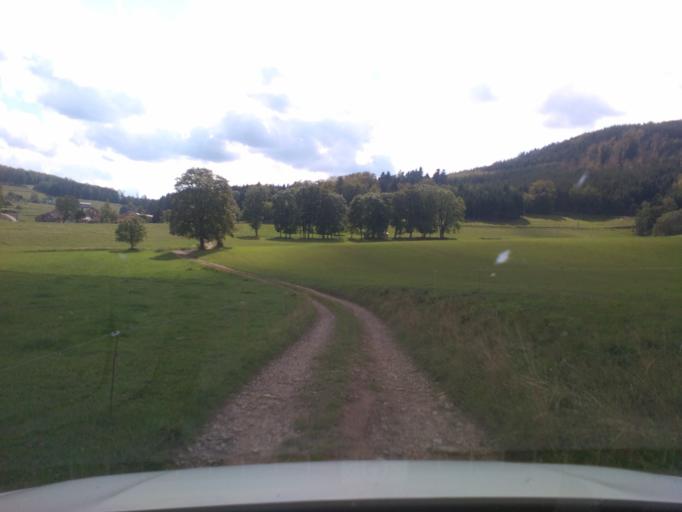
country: FR
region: Lorraine
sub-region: Departement des Vosges
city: Senones
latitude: 48.3839
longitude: 7.0197
